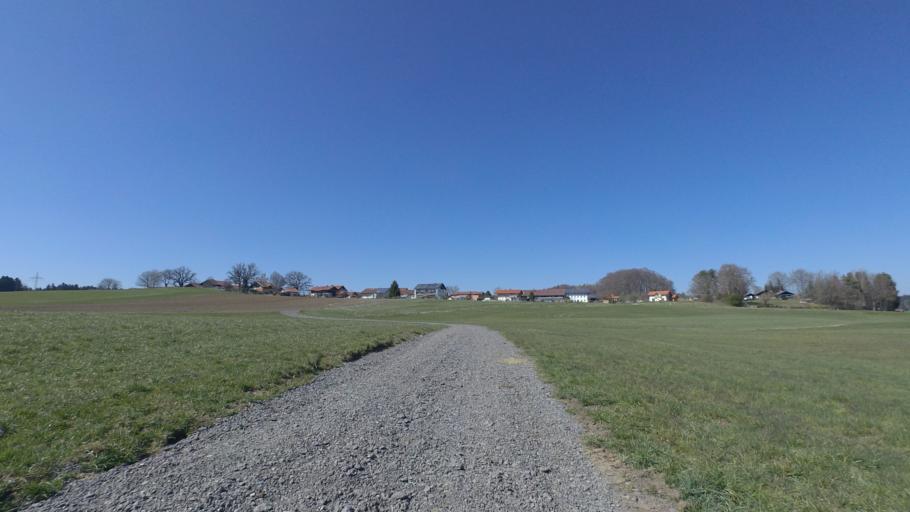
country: DE
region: Bavaria
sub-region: Upper Bavaria
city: Chieming
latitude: 47.9313
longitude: 12.5086
